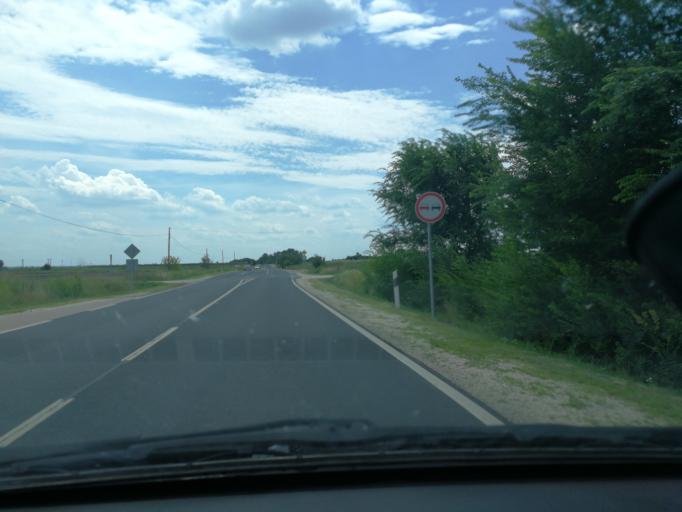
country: HU
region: Bacs-Kiskun
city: Dunapataj
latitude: 46.6143
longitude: 18.9887
